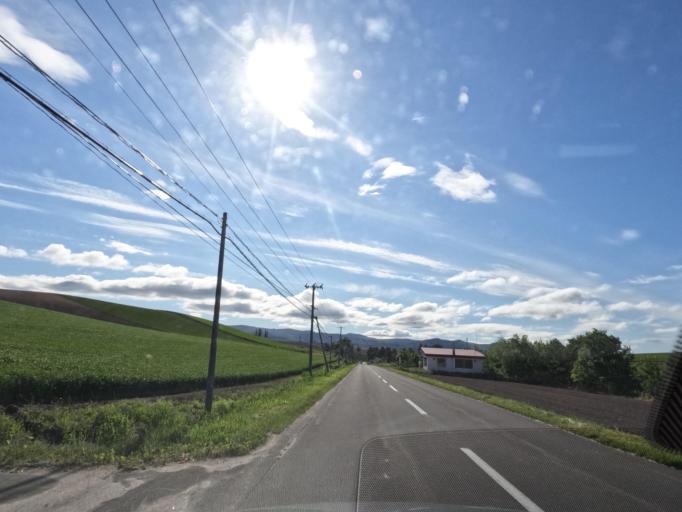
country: JP
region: Hokkaido
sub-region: Asahikawa-shi
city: Asahikawa
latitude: 43.5966
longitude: 142.4380
